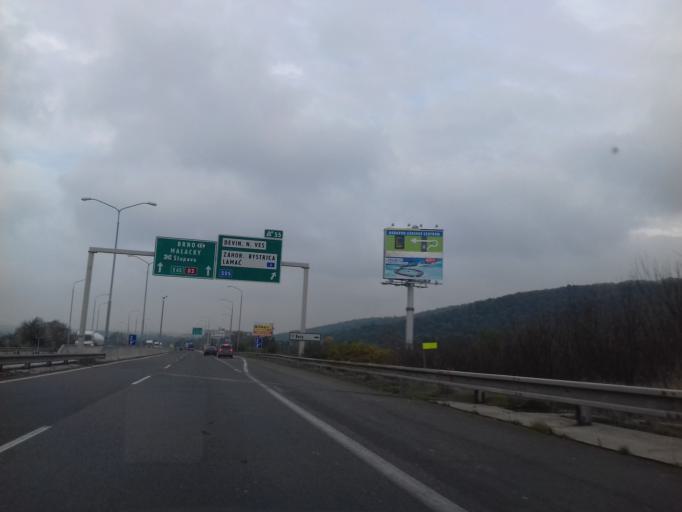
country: SK
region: Bratislavsky
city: Stupava
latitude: 48.1993
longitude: 17.0425
